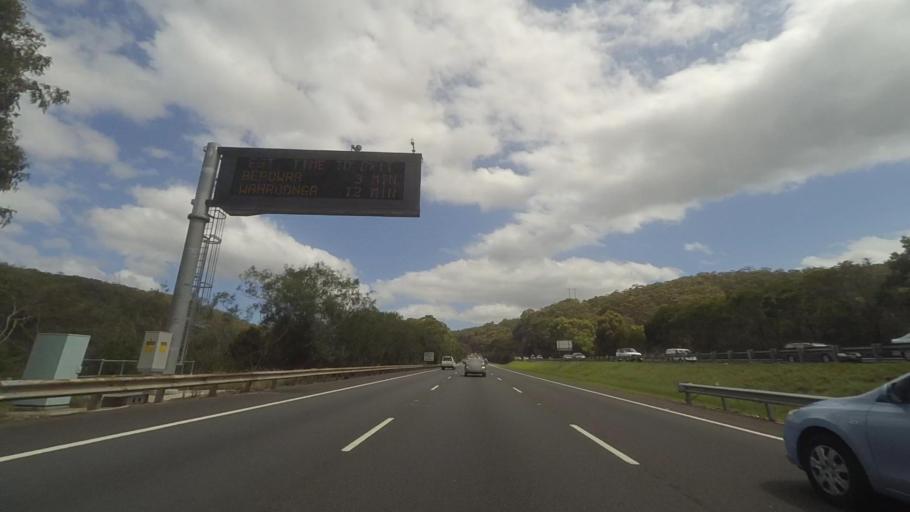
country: AU
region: New South Wales
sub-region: Hornsby Shire
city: Berowra
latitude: -33.5598
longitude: 151.1927
